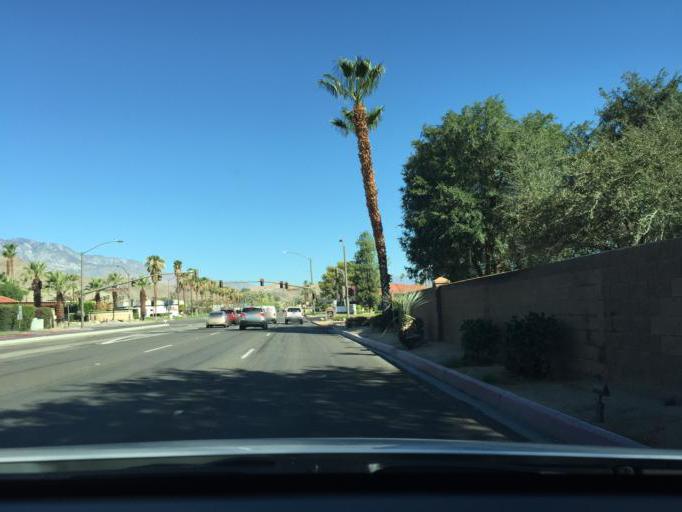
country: US
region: California
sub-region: Riverside County
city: Rancho Mirage
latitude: 33.7572
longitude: -116.4347
